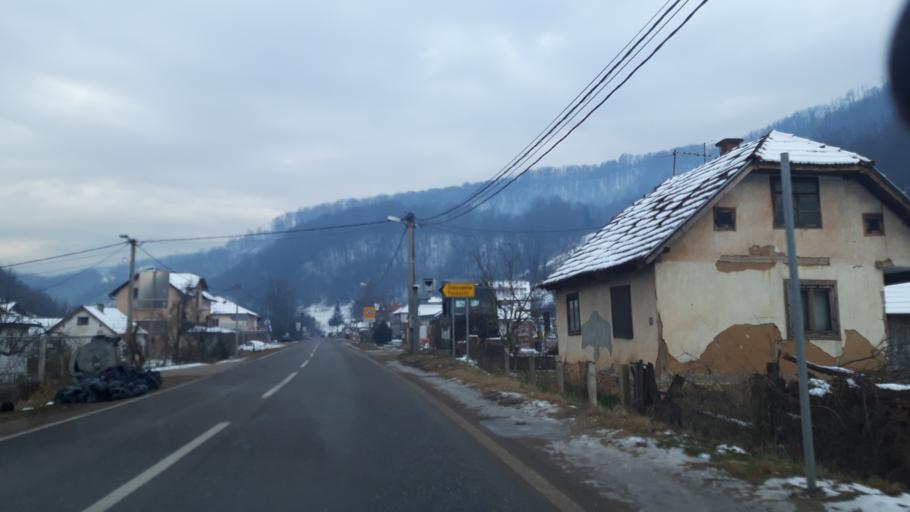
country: BA
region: Republika Srpska
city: Milici
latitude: 44.1933
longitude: 19.0719
